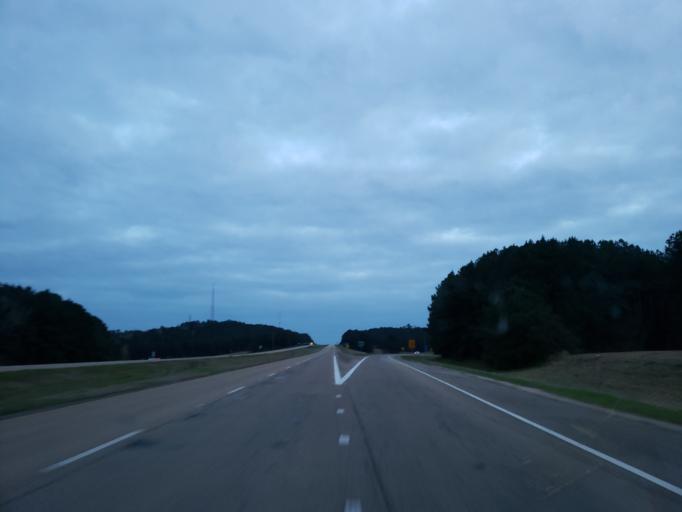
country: US
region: Mississippi
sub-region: Lauderdale County
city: Marion
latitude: 32.3720
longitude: -88.6352
